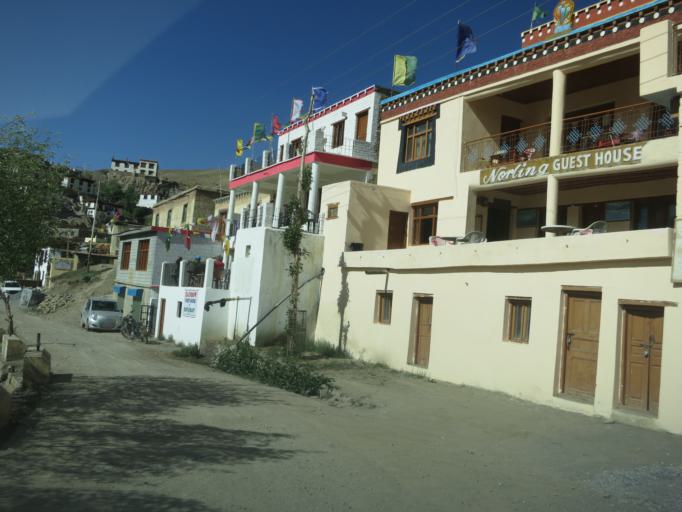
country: IN
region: Himachal Pradesh
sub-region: Kulu
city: Manali
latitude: 32.3307
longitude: 78.0088
